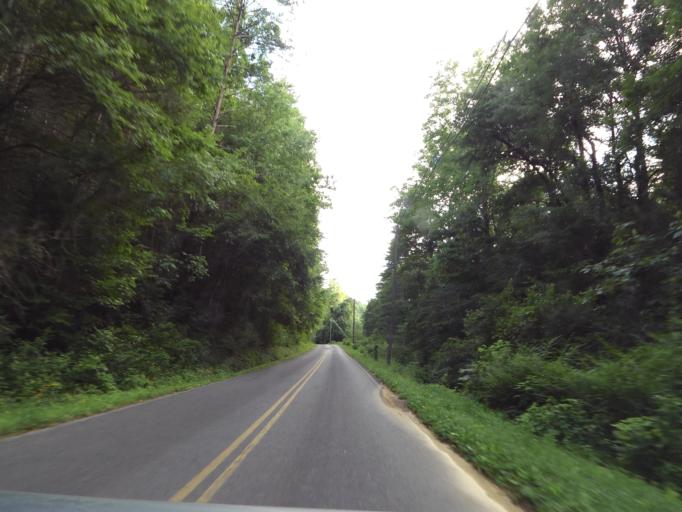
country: US
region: Tennessee
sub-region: Blount County
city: Maryville
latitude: 35.5941
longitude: -83.9765
